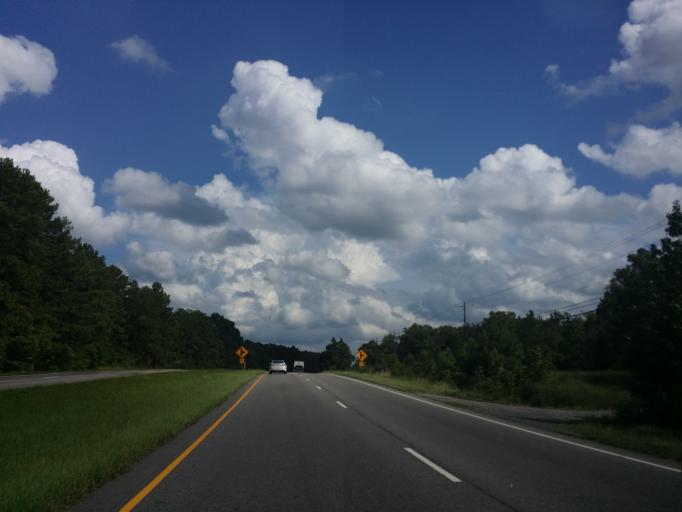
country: US
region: North Carolina
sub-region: Durham County
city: Durham
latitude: 35.9401
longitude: -78.8210
